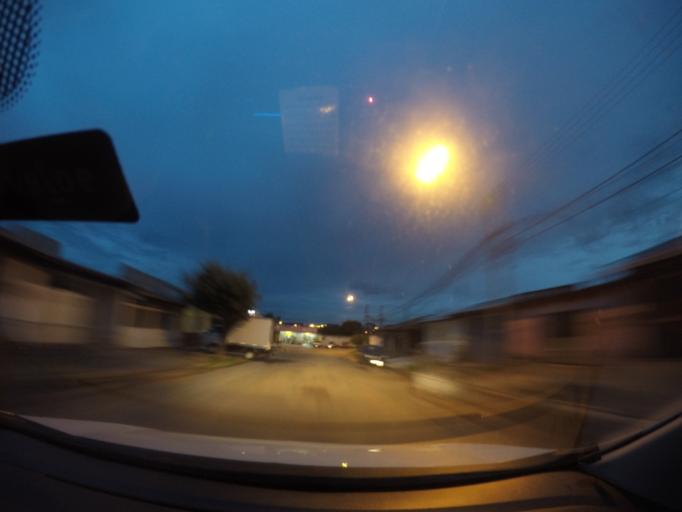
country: BR
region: Goias
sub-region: Goiania
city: Goiania
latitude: -16.7243
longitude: -49.3662
